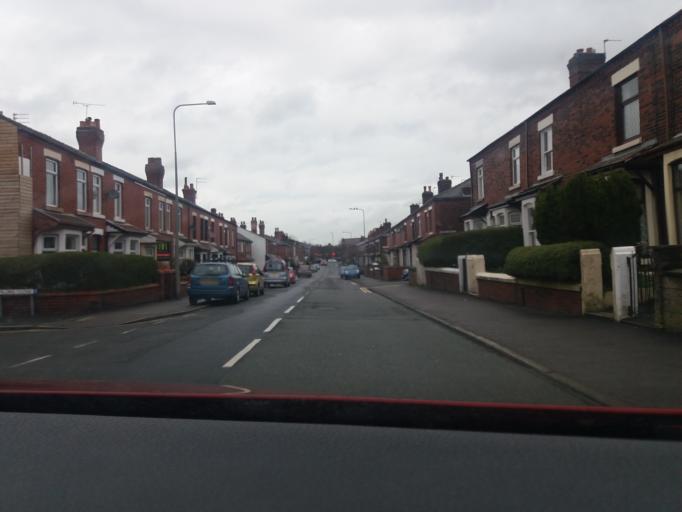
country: GB
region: England
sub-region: Lancashire
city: Chorley
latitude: 53.6448
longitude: -2.6277
